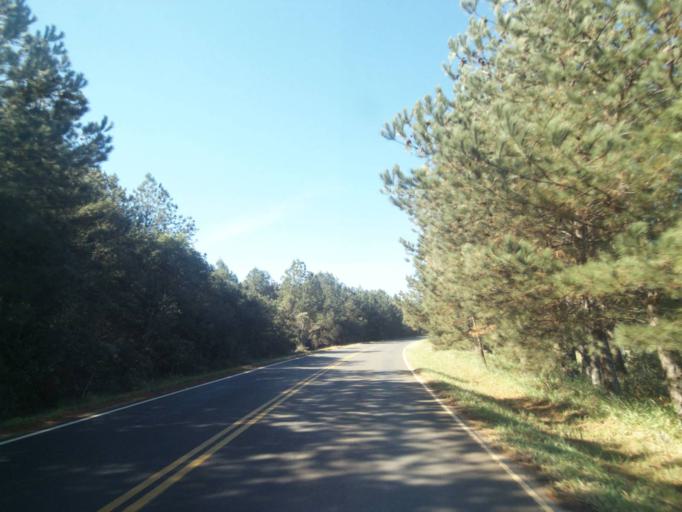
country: BR
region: Parana
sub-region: Tibagi
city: Tibagi
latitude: -24.4934
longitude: -50.4635
